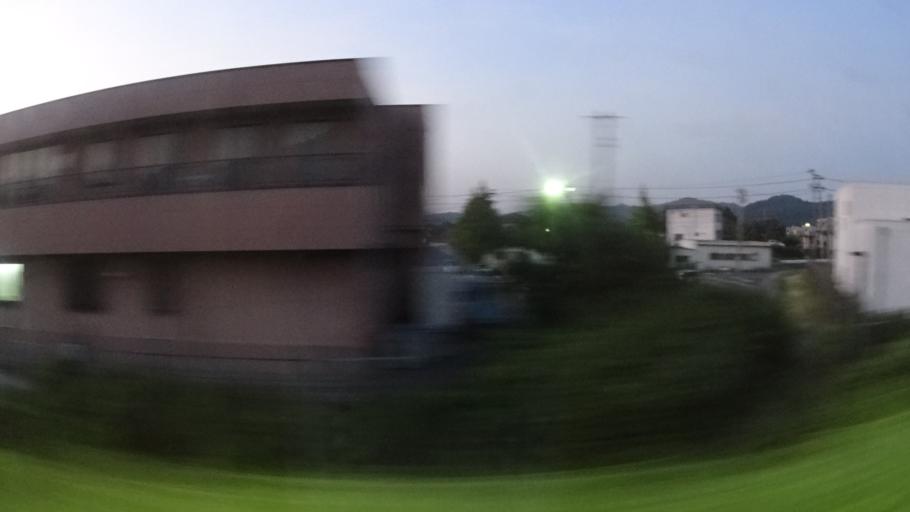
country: JP
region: Fukushima
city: Iwaki
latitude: 37.0764
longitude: 140.8703
